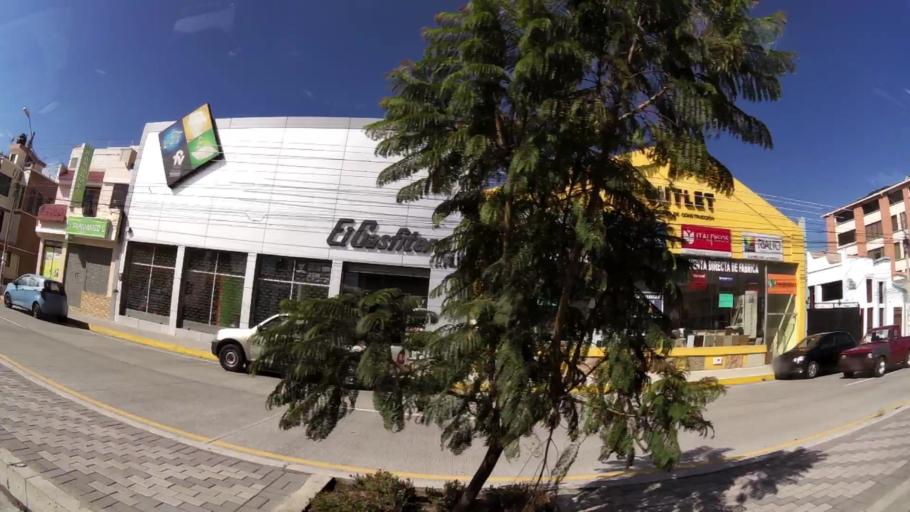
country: EC
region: Chimborazo
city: Riobamba
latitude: -1.6542
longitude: -78.6662
